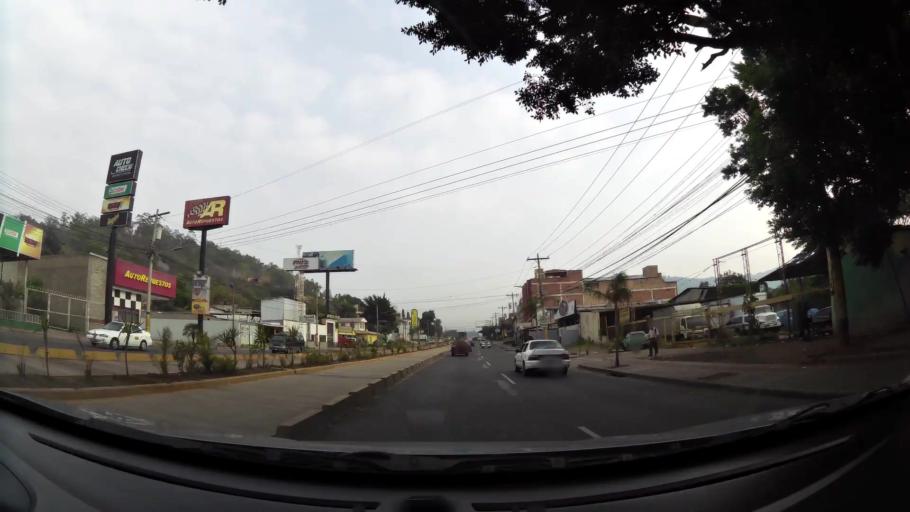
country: HN
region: Francisco Morazan
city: Tegucigalpa
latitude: 14.0909
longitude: -87.1971
